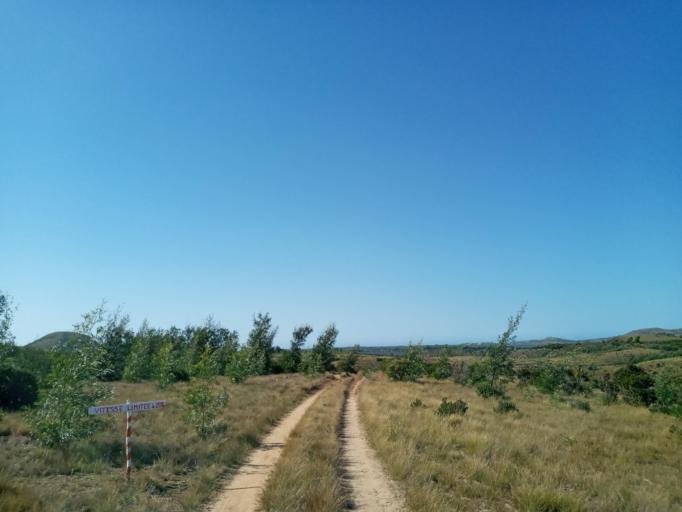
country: MG
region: Anosy
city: Fort Dauphin
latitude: -24.9137
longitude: 47.0848
